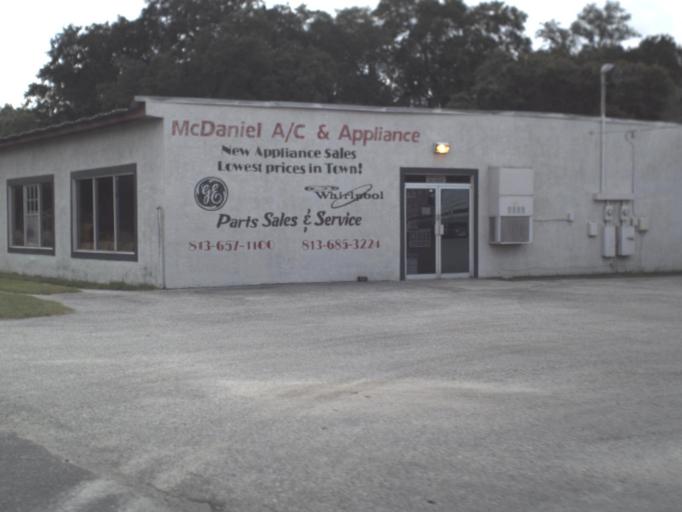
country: US
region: Florida
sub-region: Hillsborough County
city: Dover
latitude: 27.9892
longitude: -82.2474
